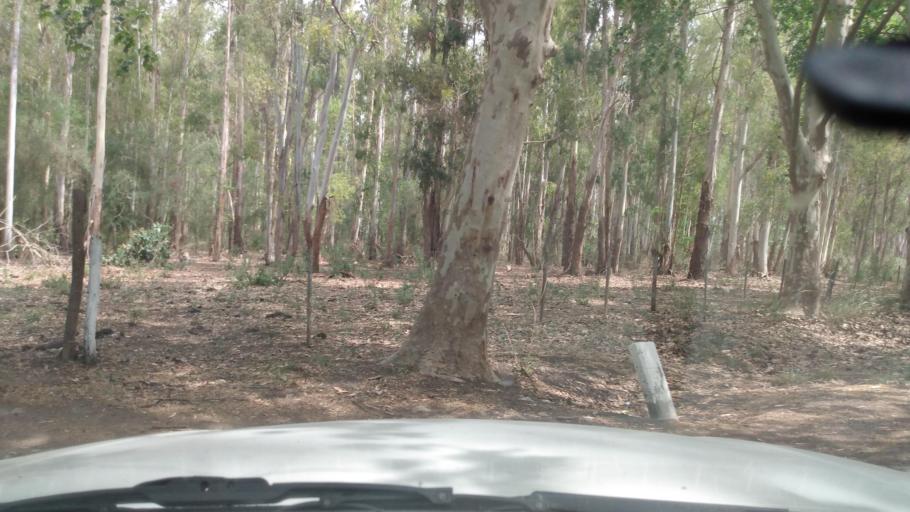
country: AR
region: Buenos Aires
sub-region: Partido de Lujan
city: Lujan
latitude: -34.5558
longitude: -59.1888
